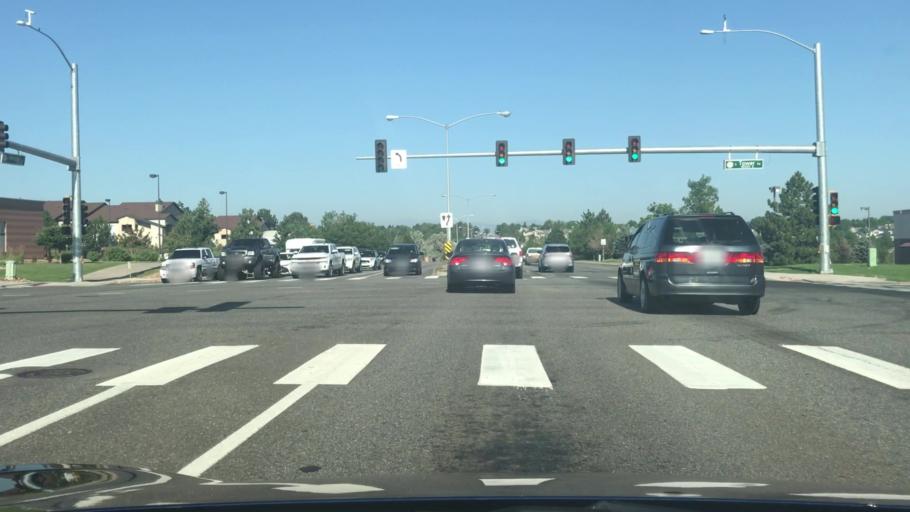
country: US
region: Colorado
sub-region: Arapahoe County
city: Dove Valley
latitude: 39.6531
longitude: -104.7722
